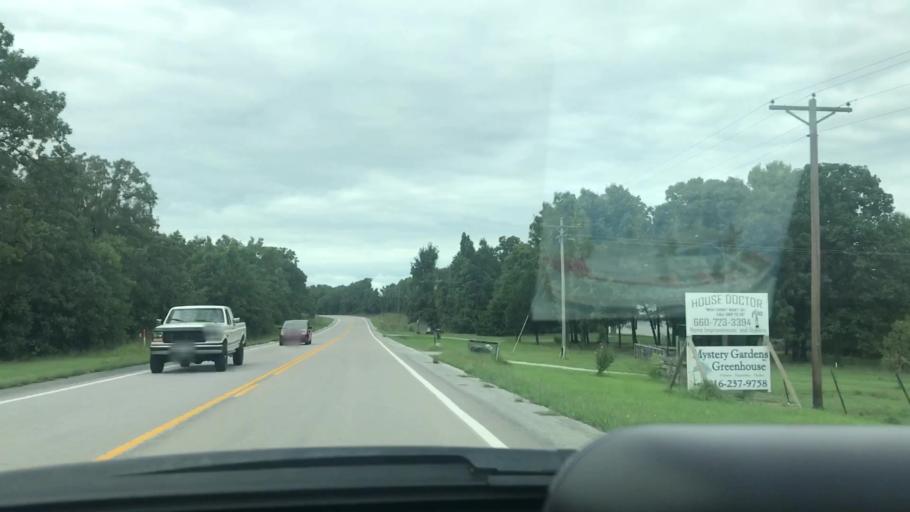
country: US
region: Missouri
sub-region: Benton County
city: Warsaw
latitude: 38.1562
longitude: -93.2968
